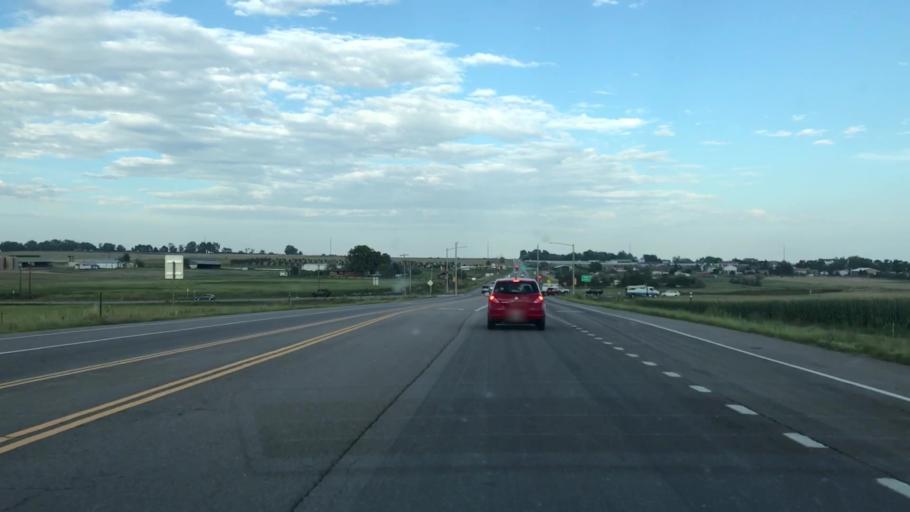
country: US
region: Colorado
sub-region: Boulder County
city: Longmont
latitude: 40.2036
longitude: -105.0576
